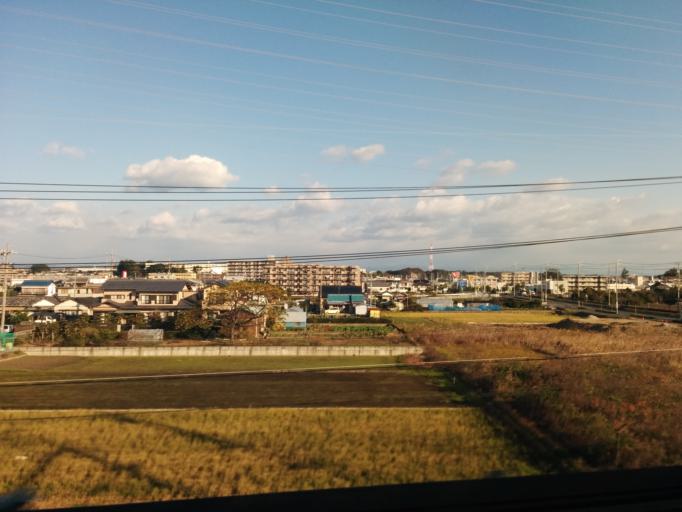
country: JP
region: Shizuoka
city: Hamamatsu
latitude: 34.6941
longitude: 137.6774
